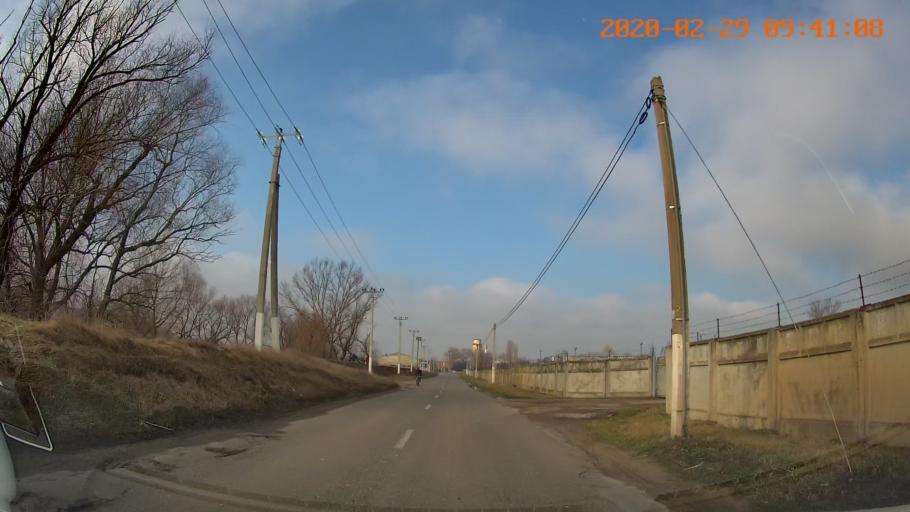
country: MD
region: Telenesti
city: Crasnoe
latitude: 46.6368
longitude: 29.8357
